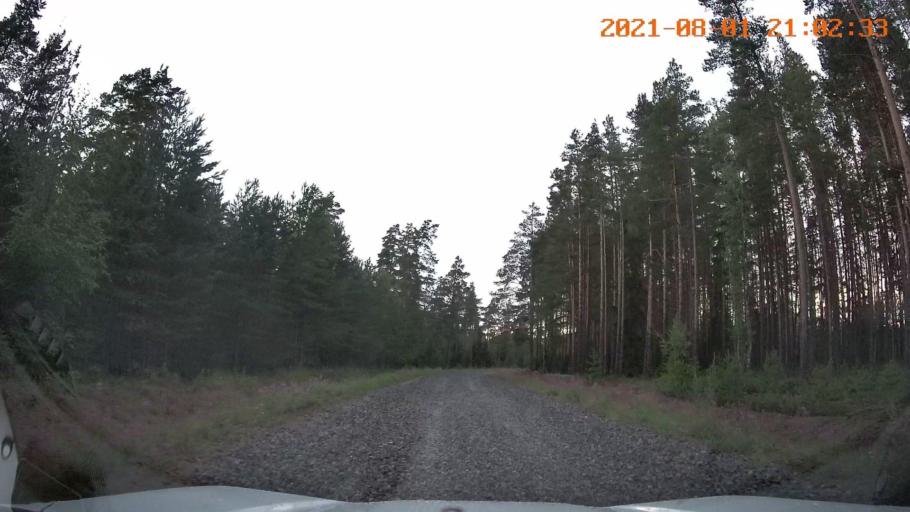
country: RU
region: Leningrad
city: Syas'stroy
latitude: 60.4883
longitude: 32.6654
